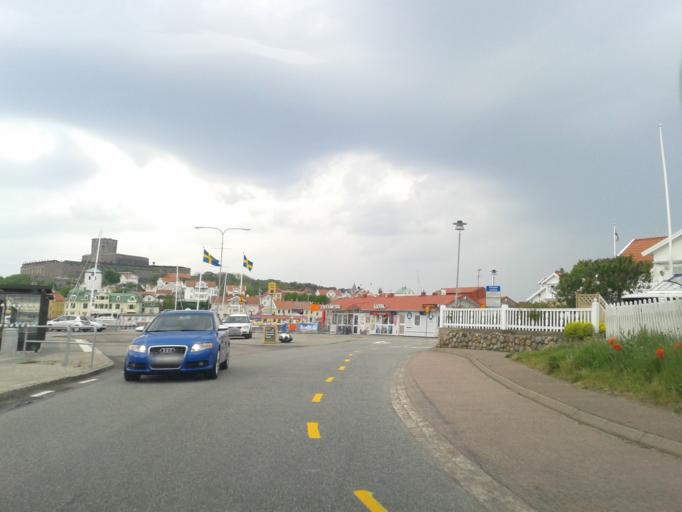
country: SE
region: Vaestra Goetaland
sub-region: Kungalvs Kommun
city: Marstrand
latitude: 57.8867
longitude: 11.5897
